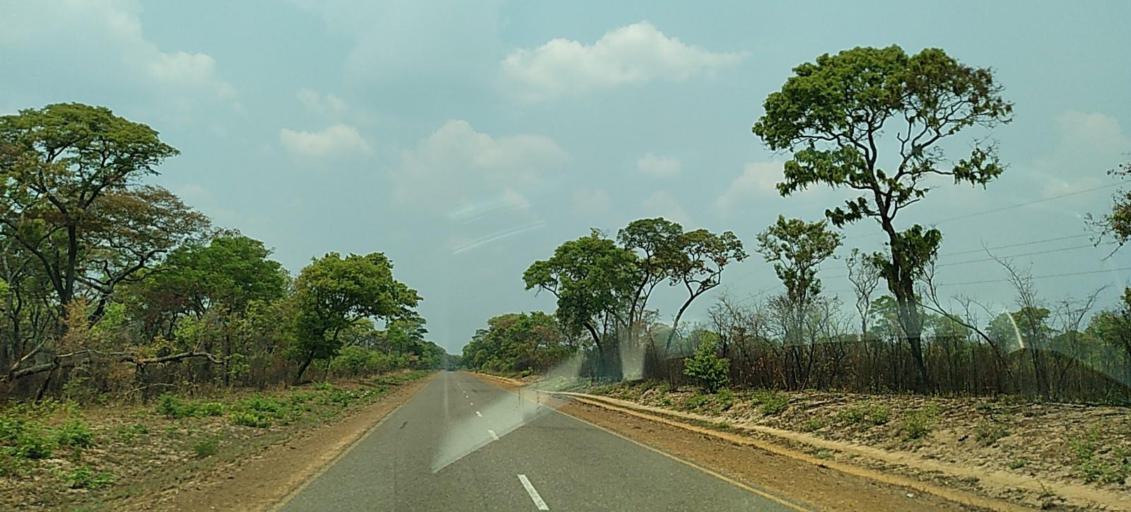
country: ZM
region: North-Western
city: Zambezi
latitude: -13.5575
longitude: 23.1990
